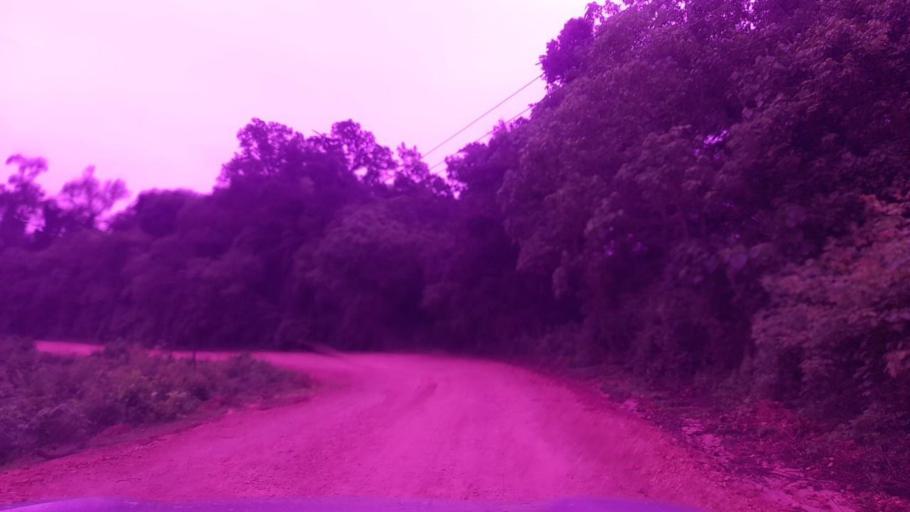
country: ET
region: Southern Nations, Nationalities, and People's Region
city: Bonga
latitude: 7.5056
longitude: 36.0987
